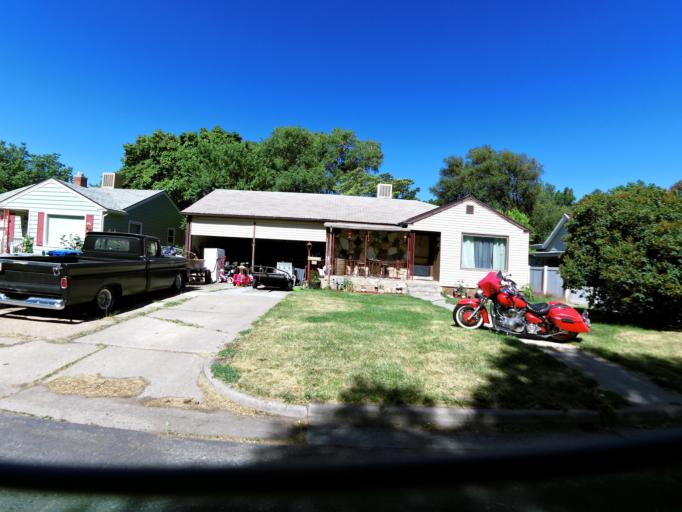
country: US
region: Utah
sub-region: Weber County
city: Ogden
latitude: 41.2279
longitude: -111.9411
